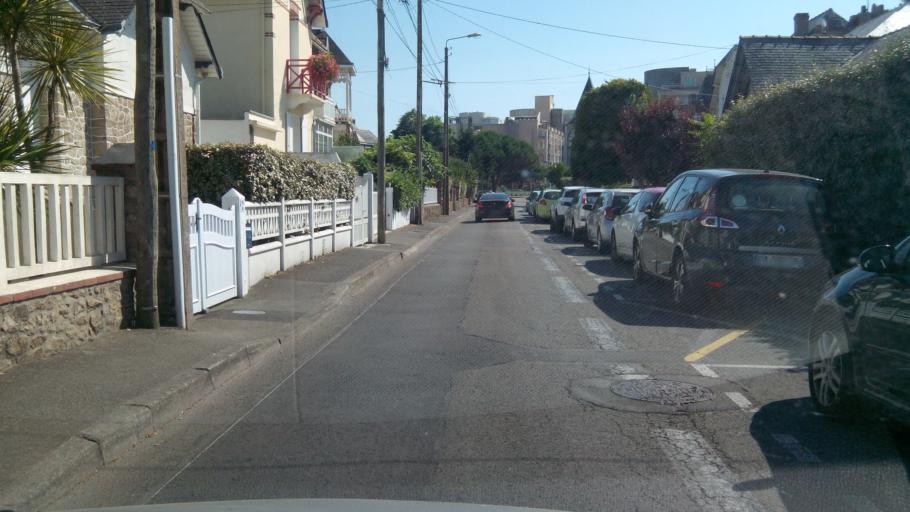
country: FR
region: Pays de la Loire
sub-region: Departement de la Loire-Atlantique
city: Pornichet
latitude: 47.2667
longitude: -2.3431
